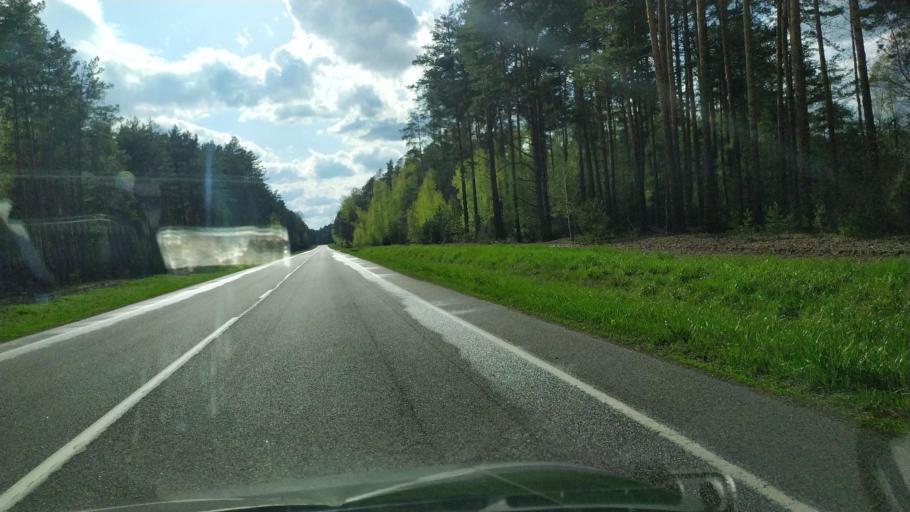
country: BY
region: Brest
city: Pruzhany
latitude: 52.7022
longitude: 24.3009
